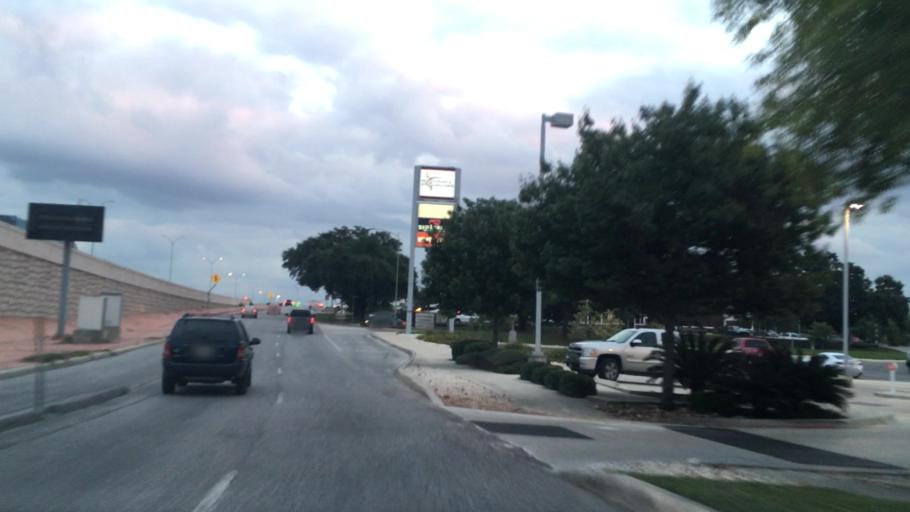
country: US
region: Texas
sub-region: Bexar County
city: Balcones Heights
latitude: 29.4892
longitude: -98.5738
